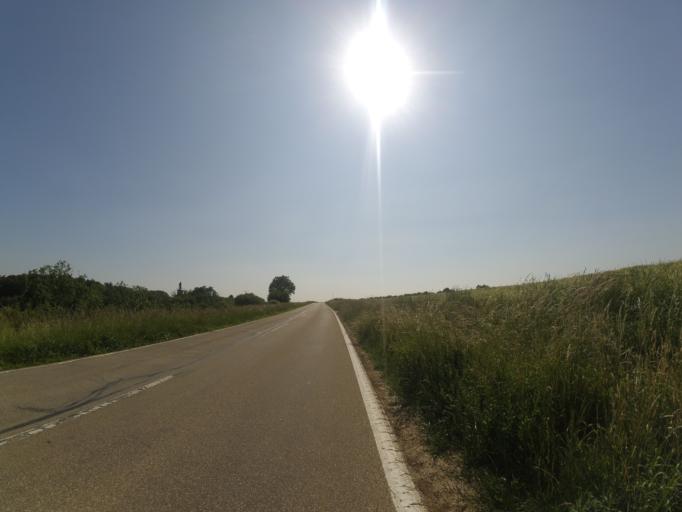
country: DE
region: Baden-Wuerttemberg
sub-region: Tuebingen Region
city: Beimerstetten
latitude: 48.4816
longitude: 10.0010
